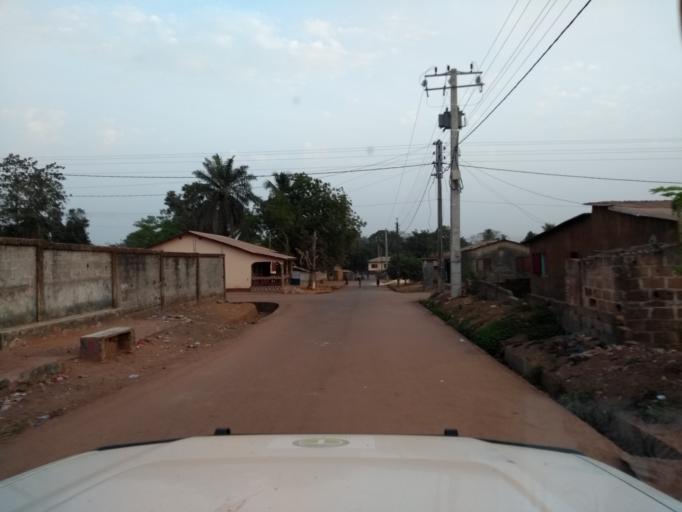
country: GN
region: Kindia
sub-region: Prefecture de Dubreka
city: Dubreka
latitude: 9.7889
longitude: -13.5238
